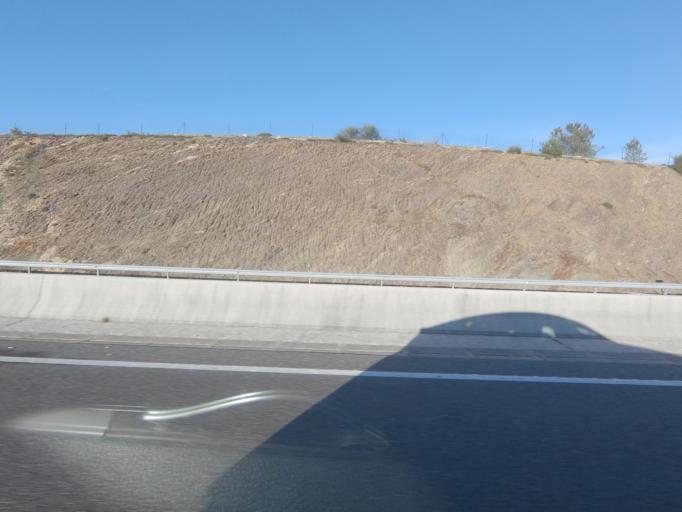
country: ES
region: Galicia
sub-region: Provincia de Pontevedra
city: Dozon
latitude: 42.5690
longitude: -8.0579
